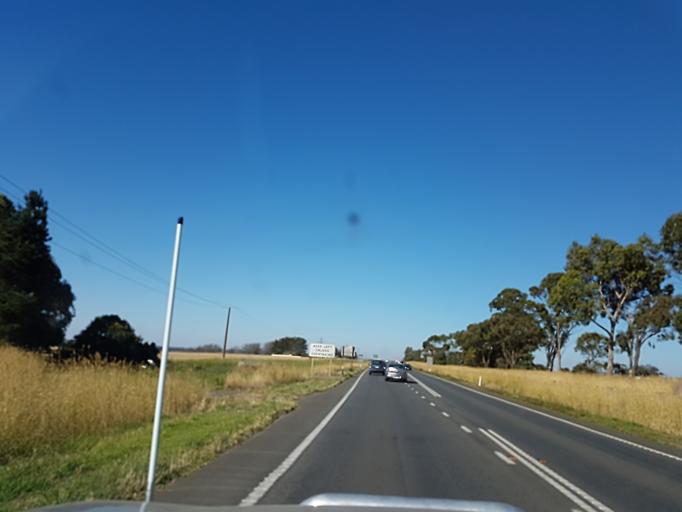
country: AU
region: Victoria
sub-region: Colac-Otway
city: Colac
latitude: -38.3229
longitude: 143.6308
